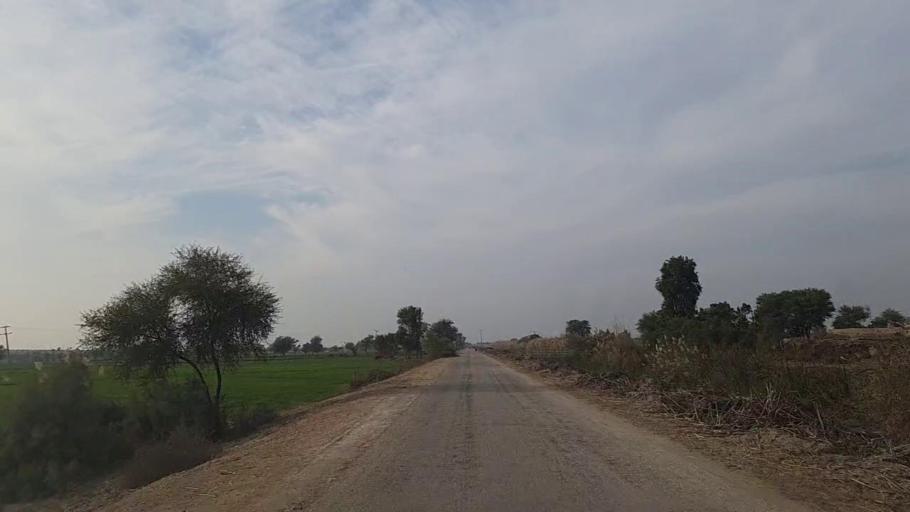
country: PK
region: Sindh
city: Daur
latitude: 26.4975
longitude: 68.4493
